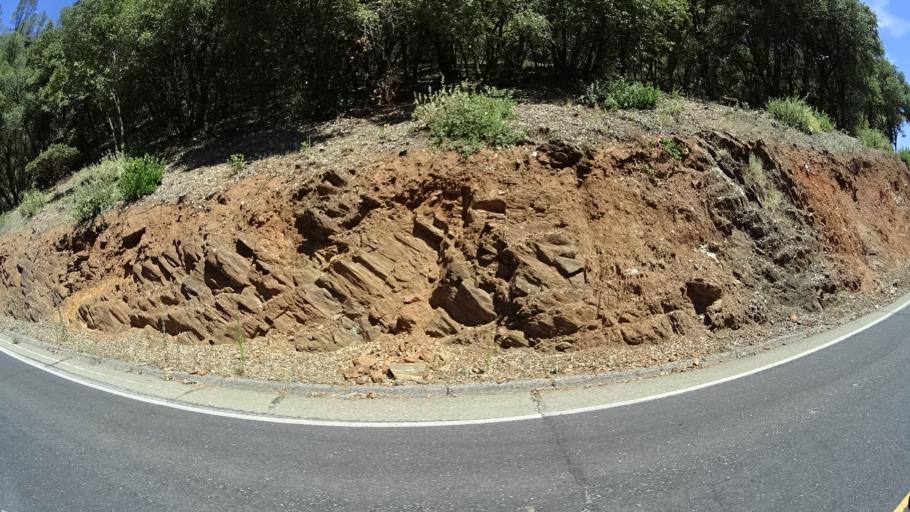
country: US
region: California
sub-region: Calaveras County
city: Murphys
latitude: 38.1319
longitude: -120.4818
